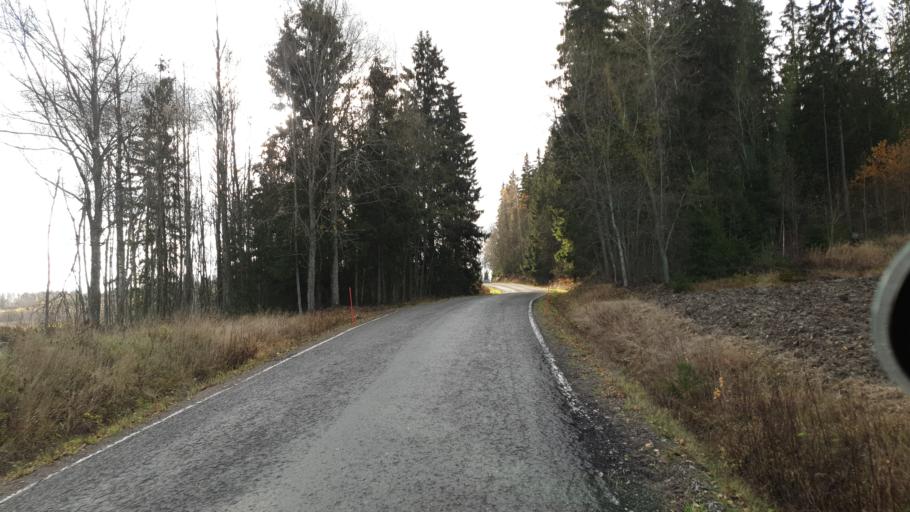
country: FI
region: Uusimaa
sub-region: Helsinki
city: Siuntio
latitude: 60.2518
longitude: 24.2986
